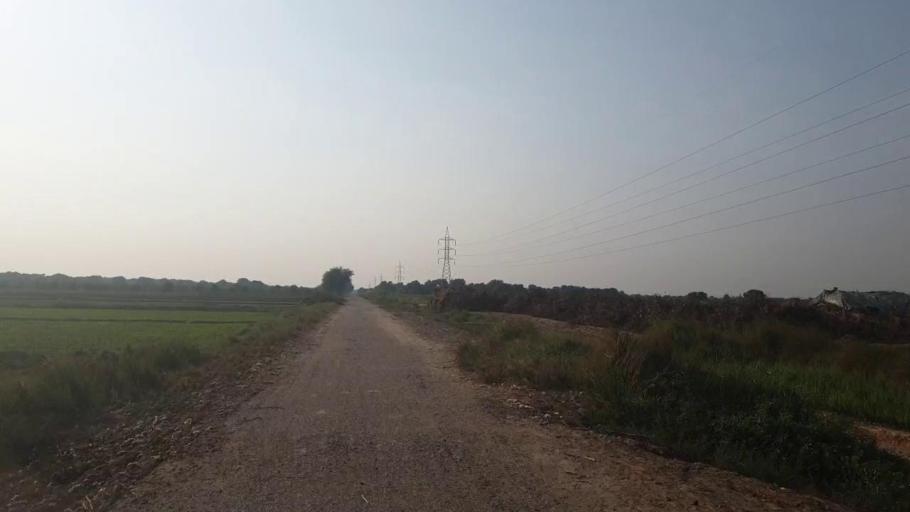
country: PK
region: Sindh
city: Tando Jam
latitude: 25.4267
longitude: 68.4762
